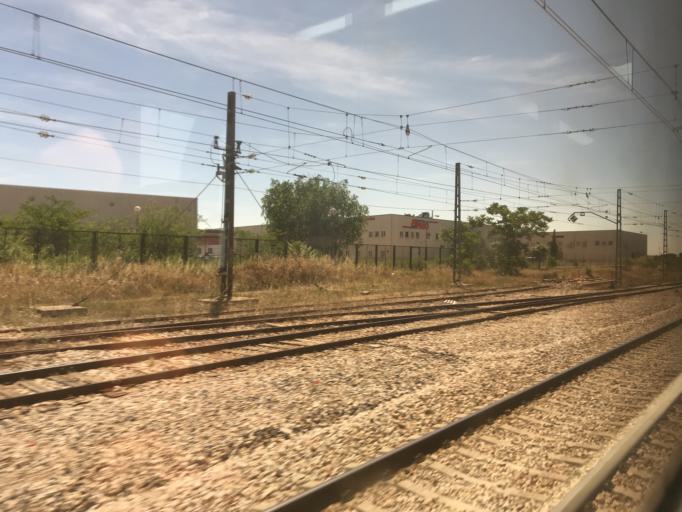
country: ES
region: Madrid
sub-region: Provincia de Madrid
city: Getafe
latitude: 40.3047
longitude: -3.7074
